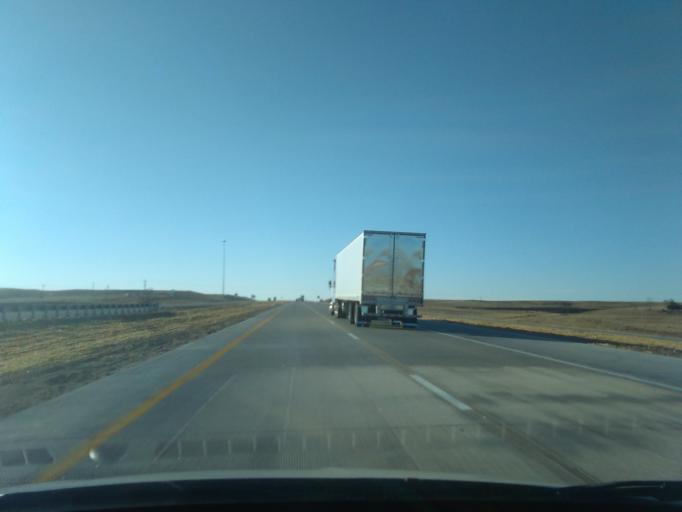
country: US
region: Nebraska
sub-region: Deuel County
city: Chappell
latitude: 41.1138
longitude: -102.6302
